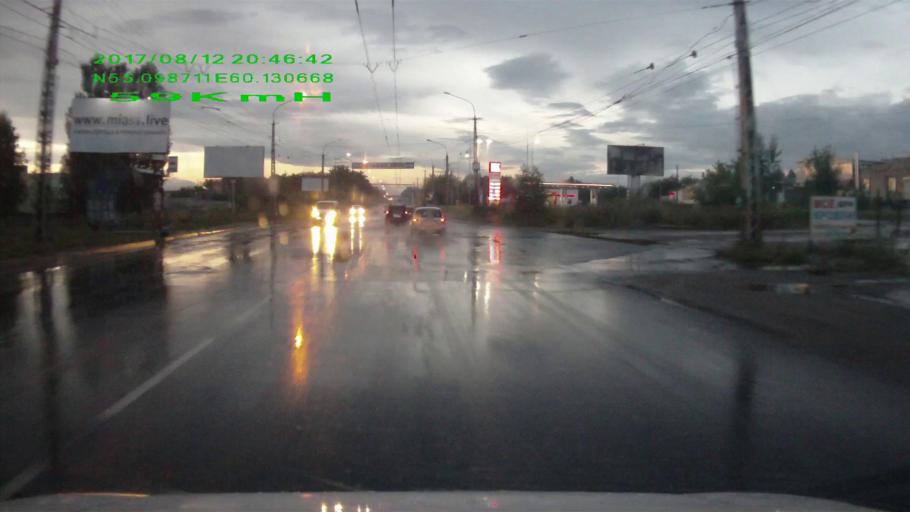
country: RU
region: Chelyabinsk
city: Turgoyak
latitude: 55.0987
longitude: 60.1307
